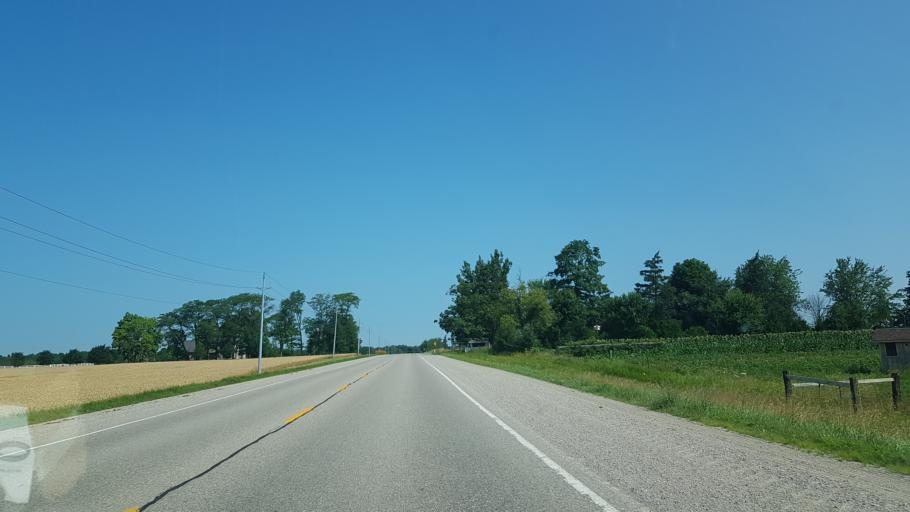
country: CA
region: Ontario
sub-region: Oxford County
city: Woodstock
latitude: 42.9396
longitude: -80.6778
